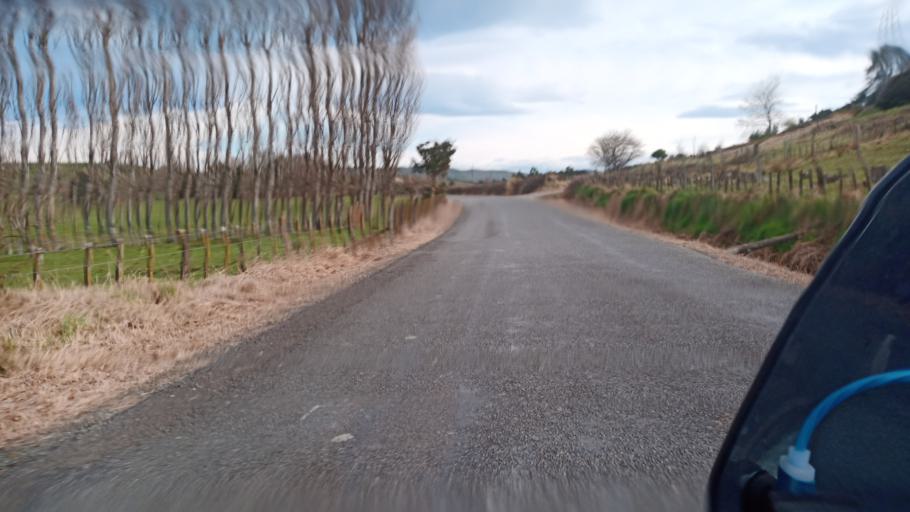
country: NZ
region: Hawke's Bay
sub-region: Wairoa District
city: Wairoa
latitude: -38.9738
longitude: 177.4300
